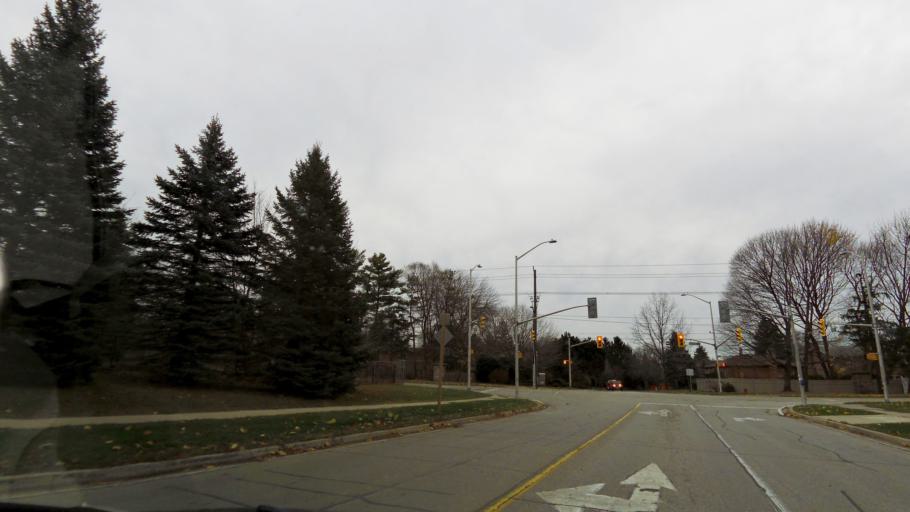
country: CA
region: Ontario
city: Oakville
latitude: 43.4762
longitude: -79.6361
